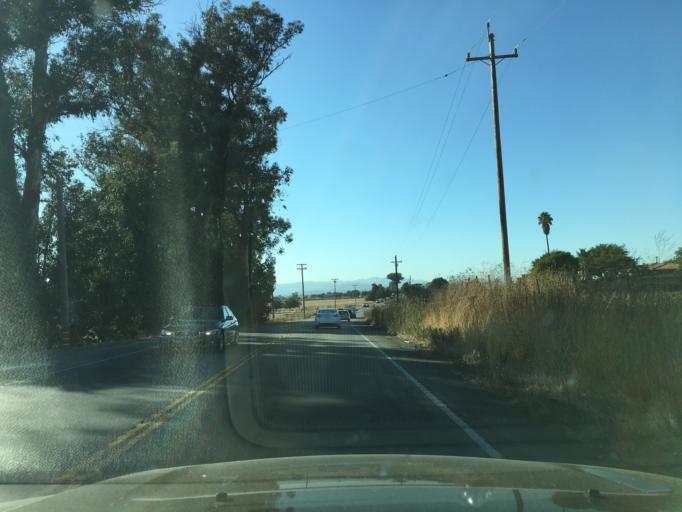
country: US
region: California
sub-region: Santa Clara County
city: Gilroy
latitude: 36.9855
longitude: -121.4829
